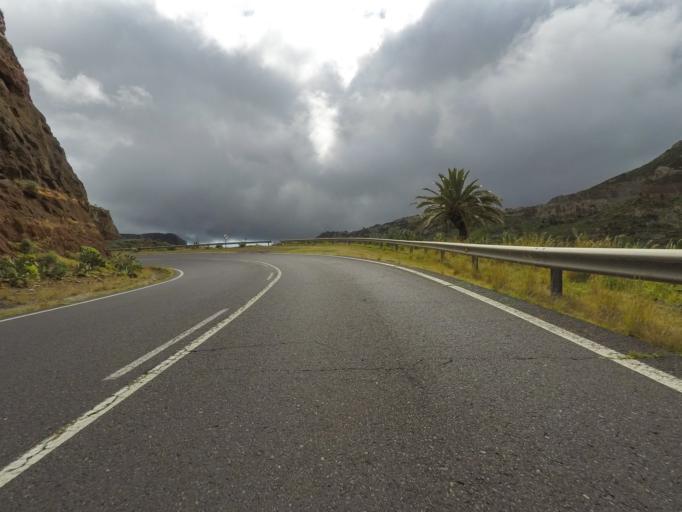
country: ES
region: Canary Islands
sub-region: Provincia de Santa Cruz de Tenerife
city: Alajero
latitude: 28.0947
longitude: -17.1991
